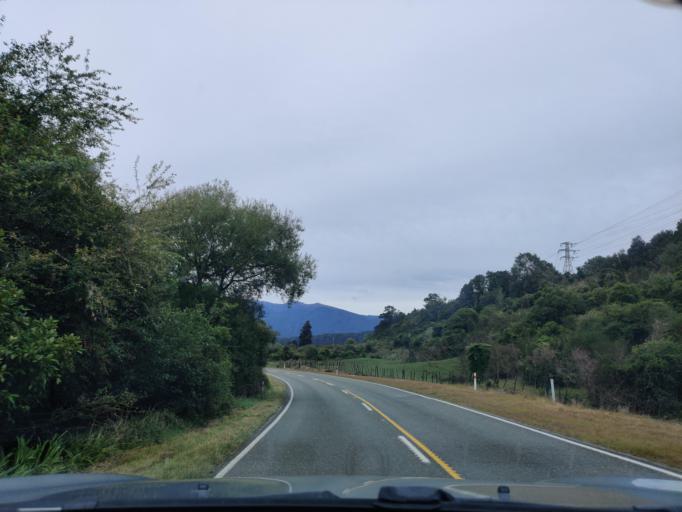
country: NZ
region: West Coast
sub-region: Buller District
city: Westport
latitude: -41.8412
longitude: 171.9334
